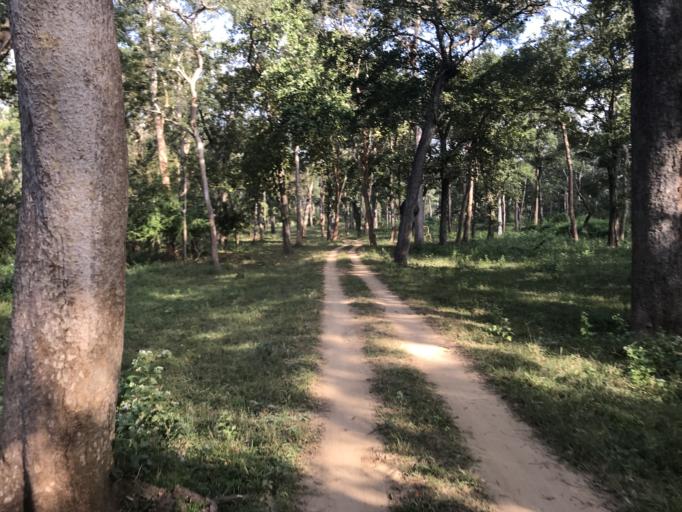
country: IN
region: Karnataka
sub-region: Mysore
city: Heggadadevankote
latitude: 11.9498
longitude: 76.1939
